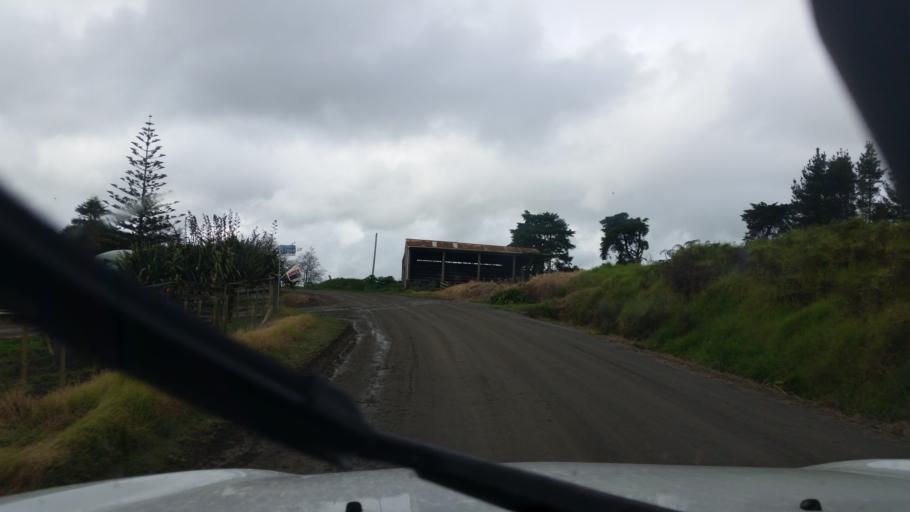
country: NZ
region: Northland
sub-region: Whangarei
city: Maungatapere
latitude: -35.6158
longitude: 174.1960
